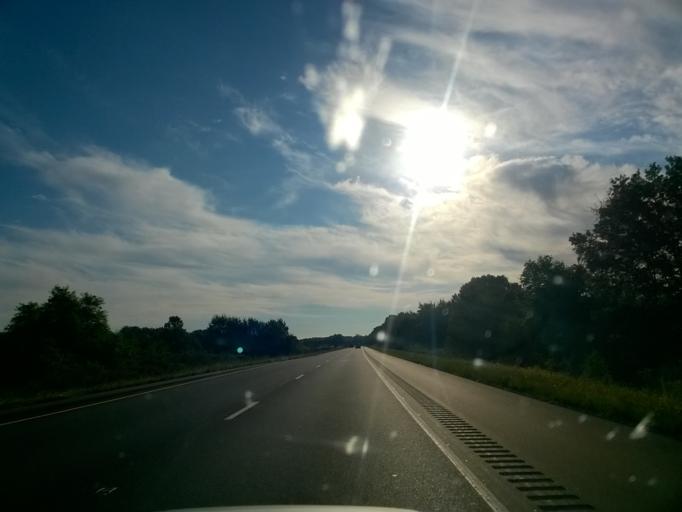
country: US
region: Indiana
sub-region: Warrick County
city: Chandler
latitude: 38.1834
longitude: -87.3828
